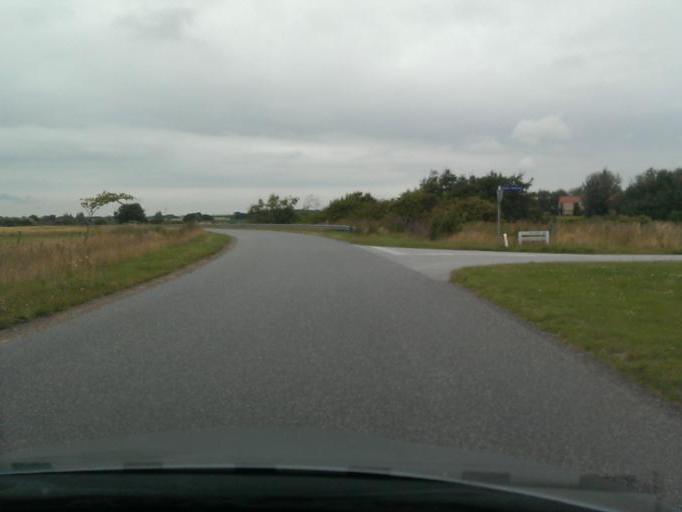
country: DK
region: North Denmark
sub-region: Hjorring Kommune
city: Vra
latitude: 57.3536
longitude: 9.9311
